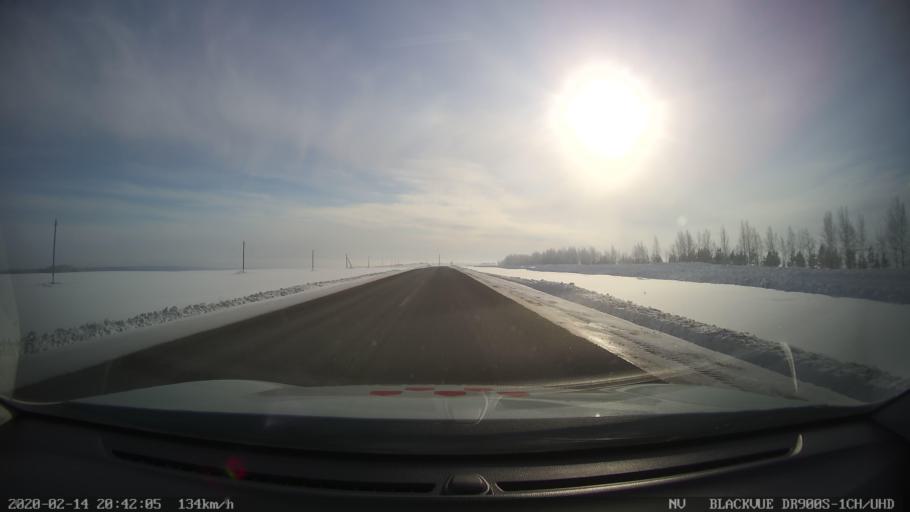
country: RU
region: Tatarstan
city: Kuybyshevskiy Zaton
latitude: 55.3212
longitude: 49.1359
